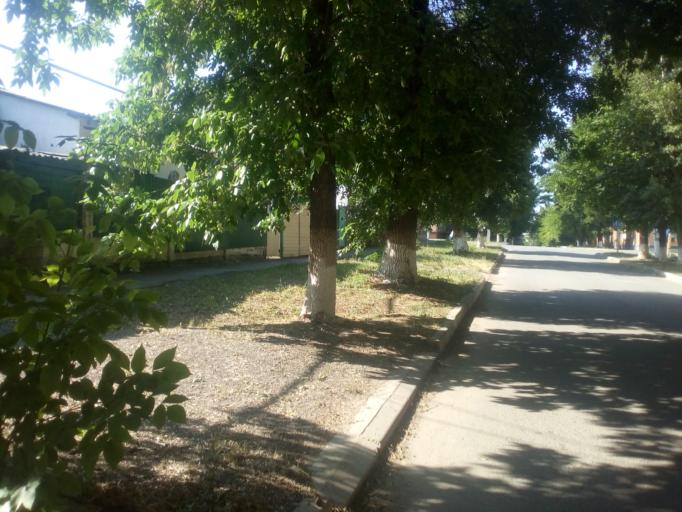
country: RU
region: Rostov
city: Sholokhovskiy
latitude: 48.2812
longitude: 41.0546
